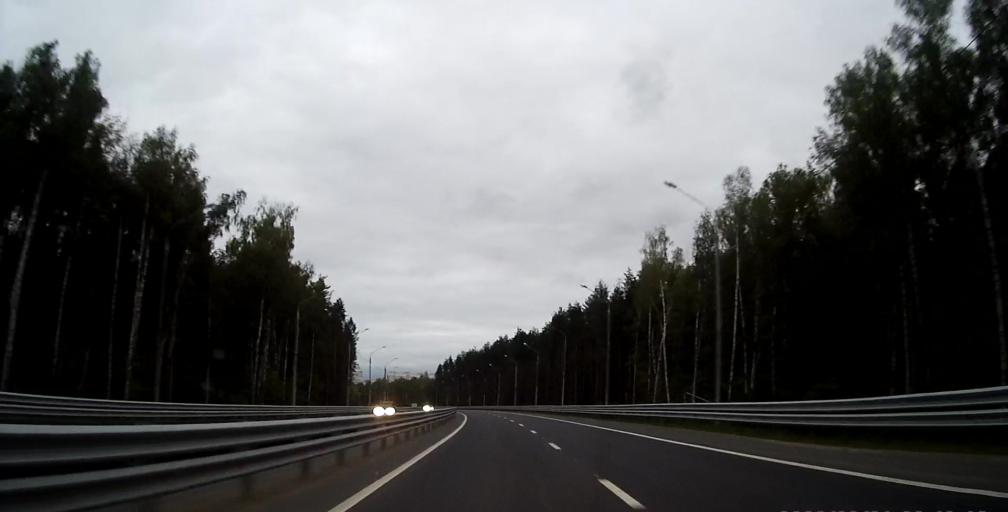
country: RU
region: Moskovskaya
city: Dubrovitsy
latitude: 55.4037
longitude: 37.5006
